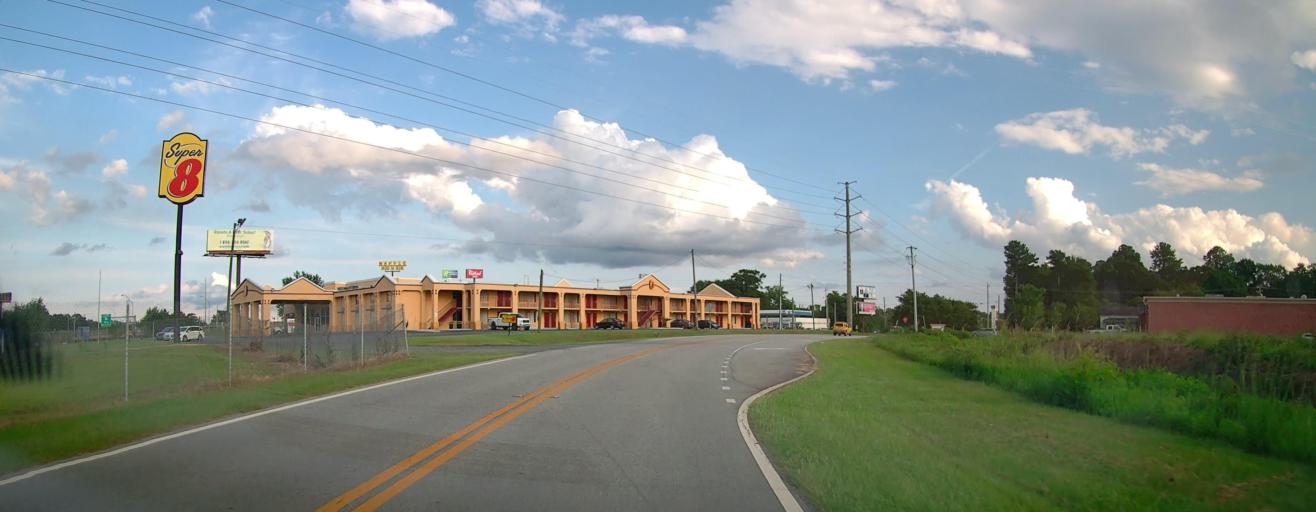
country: US
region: Georgia
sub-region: Monroe County
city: Forsyth
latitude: 33.0361
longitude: -83.9257
